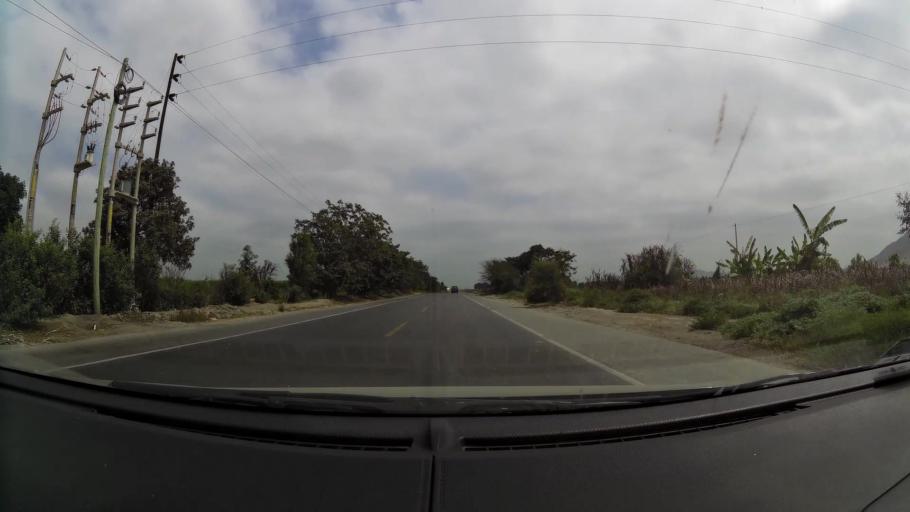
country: PE
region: La Libertad
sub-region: Ascope
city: Chocope
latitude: -7.8027
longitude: -79.1968
